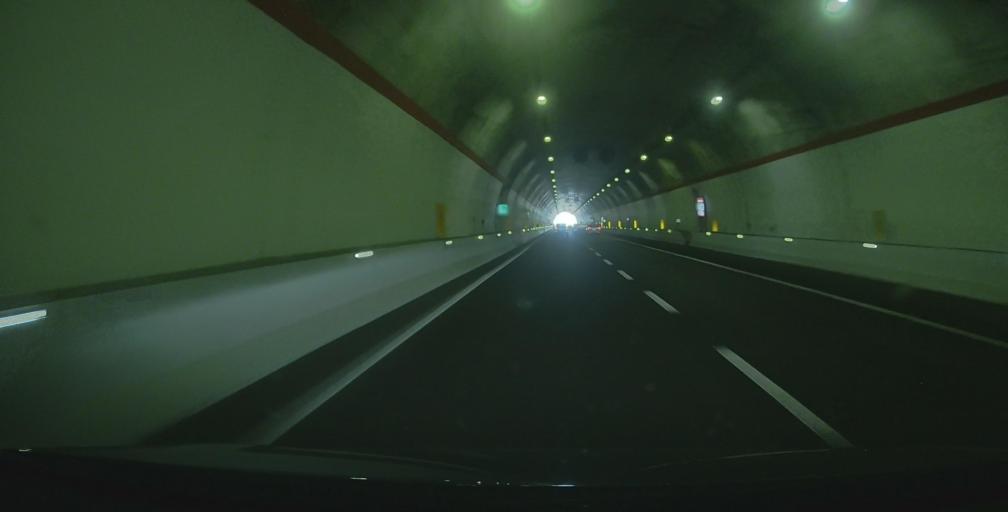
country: IT
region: Calabria
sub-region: Provincia di Cosenza
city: Morano Calabro
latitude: 39.8739
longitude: 16.1249
